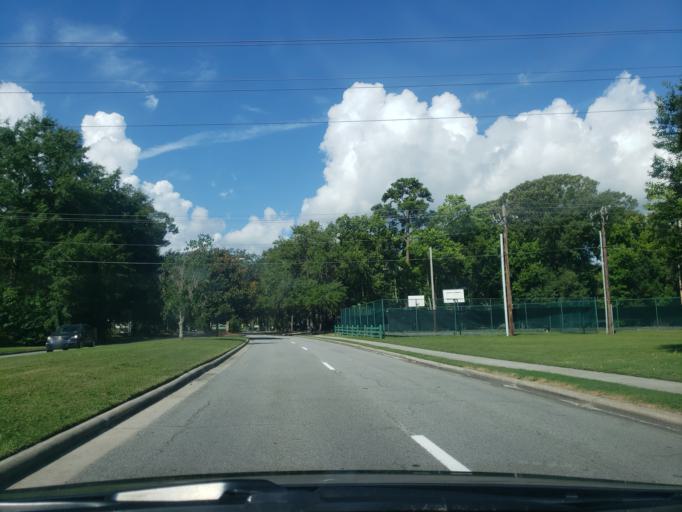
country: US
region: Georgia
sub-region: Chatham County
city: Georgetown
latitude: 31.9827
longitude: -81.2238
